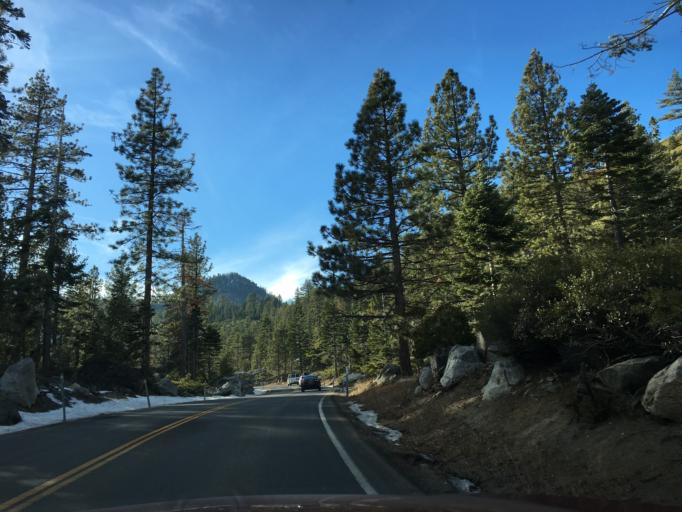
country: US
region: California
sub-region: El Dorado County
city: South Lake Tahoe
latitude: 38.9497
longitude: -120.0859
